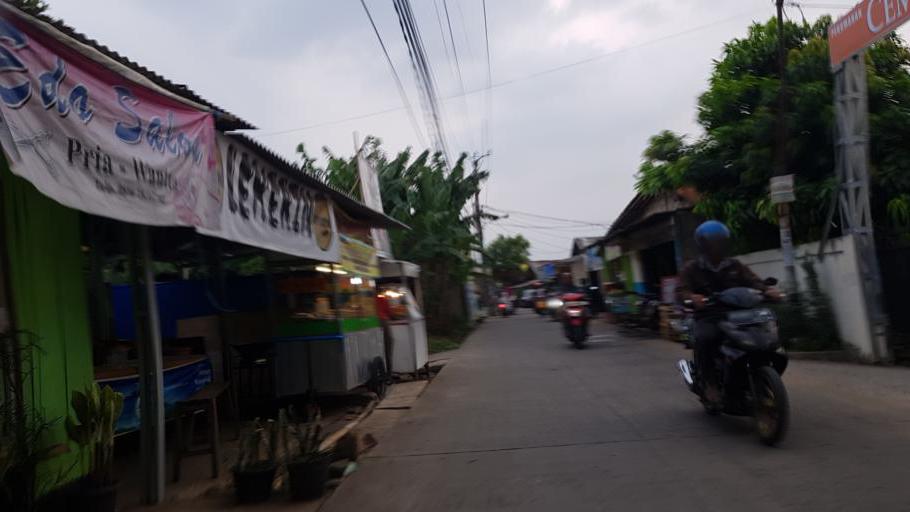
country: ID
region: West Java
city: Sawangan
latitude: -6.3798
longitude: 106.7936
